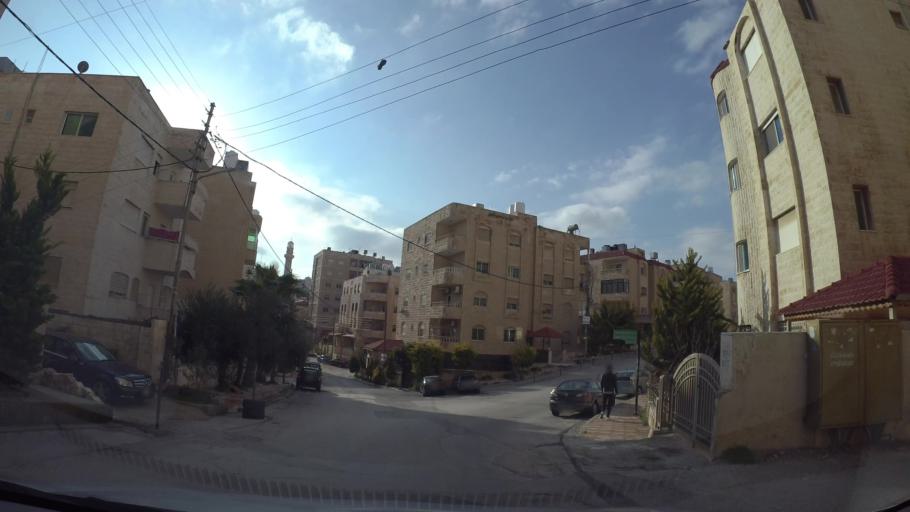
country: JO
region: Amman
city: Al Jubayhah
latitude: 32.0023
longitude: 35.8659
